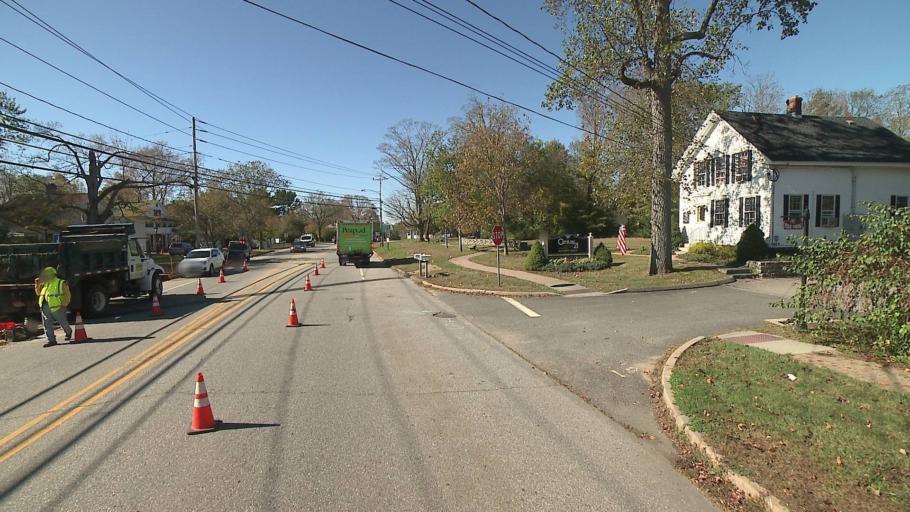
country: US
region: Connecticut
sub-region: Tolland County
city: Hebron
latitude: 41.6586
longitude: -72.3642
